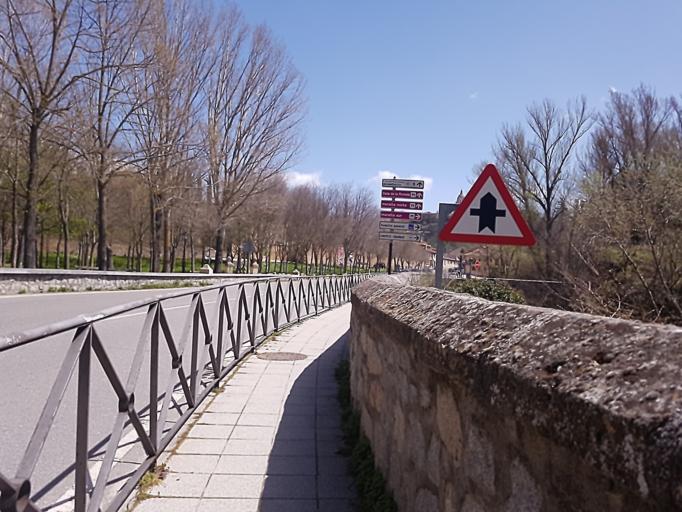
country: ES
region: Castille and Leon
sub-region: Provincia de Segovia
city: Segovia
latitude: 40.9559
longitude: -4.1356
